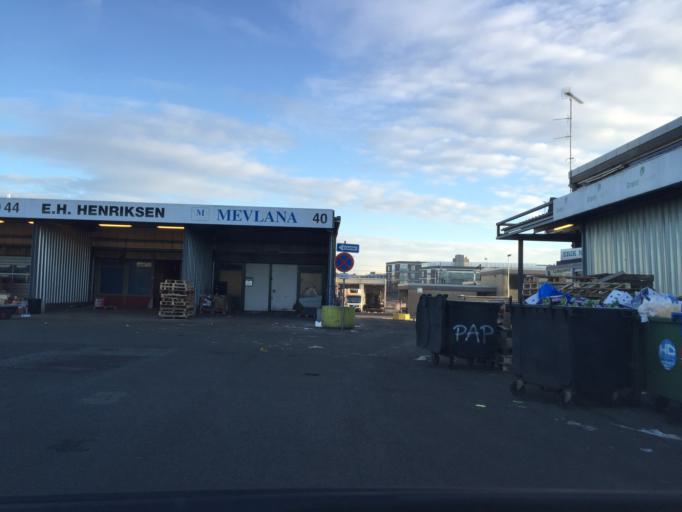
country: DK
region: Capital Region
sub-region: Hvidovre Kommune
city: Hvidovre
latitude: 55.6550
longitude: 12.5081
